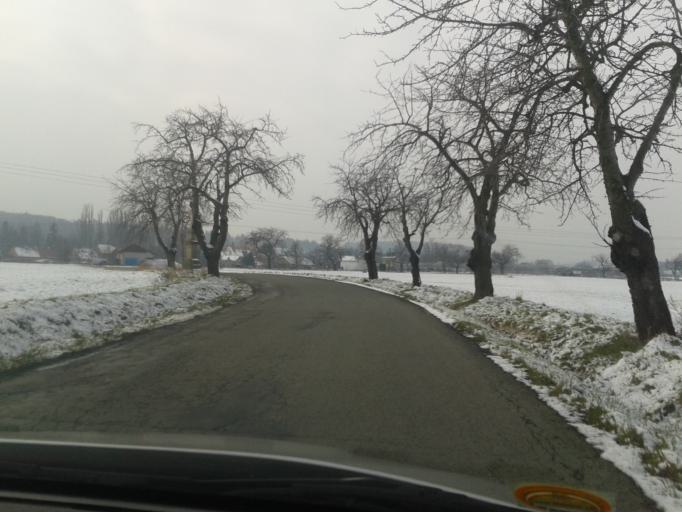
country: CZ
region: Olomoucky
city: Mostkovice
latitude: 49.4767
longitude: 17.0539
